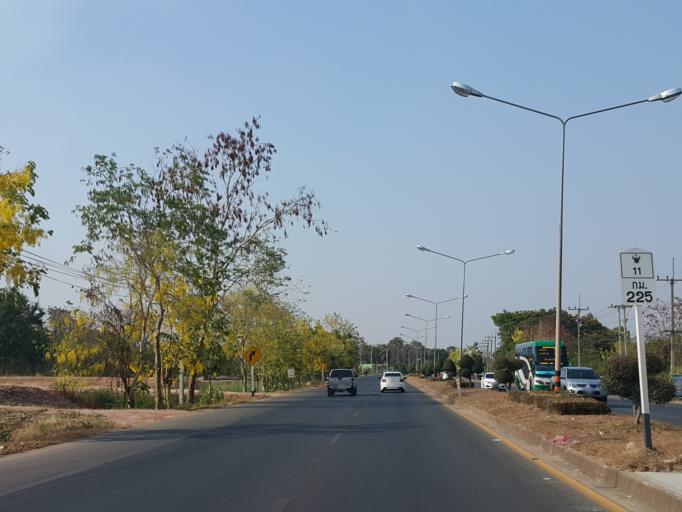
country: TH
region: Phitsanulok
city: Phitsanulok
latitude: 16.8287
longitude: 100.3326
